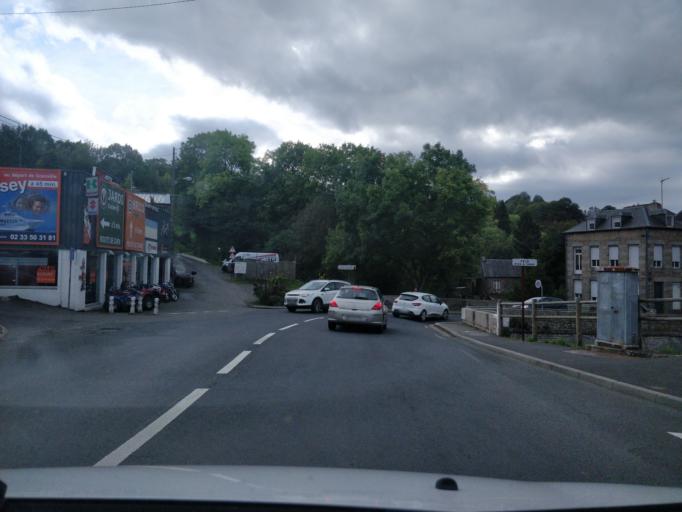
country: FR
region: Lower Normandy
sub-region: Departement du Calvados
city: Vire
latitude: 48.8455
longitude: -0.8966
